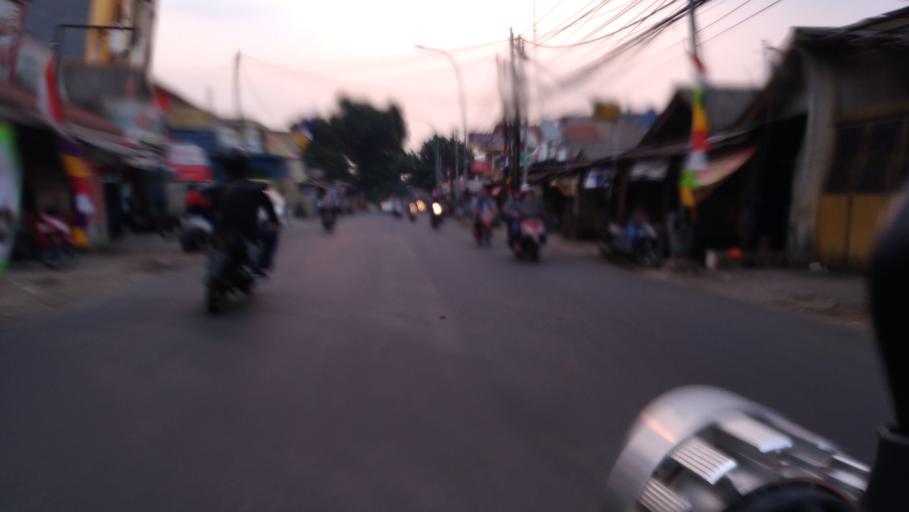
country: ID
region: West Java
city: Depok
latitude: -6.3481
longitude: 106.8761
